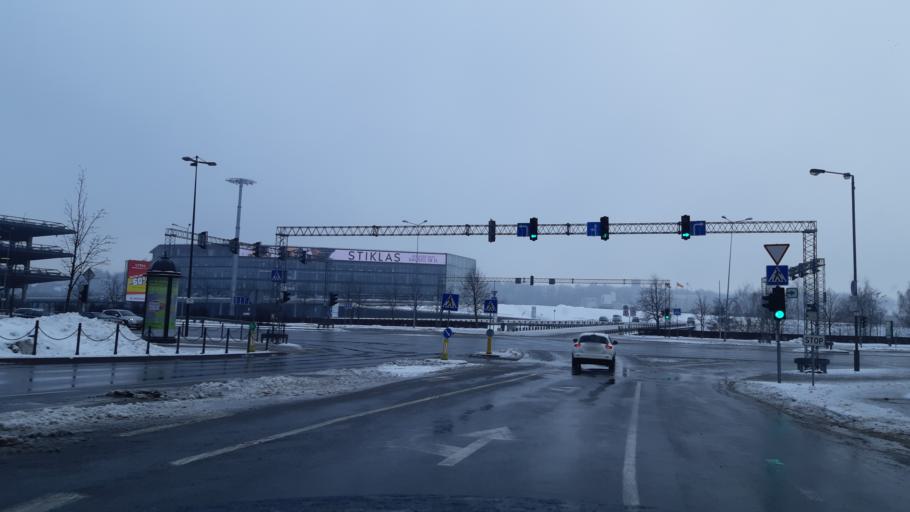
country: LT
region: Kauno apskritis
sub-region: Kaunas
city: Kaunas
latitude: 54.8930
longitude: 23.9170
